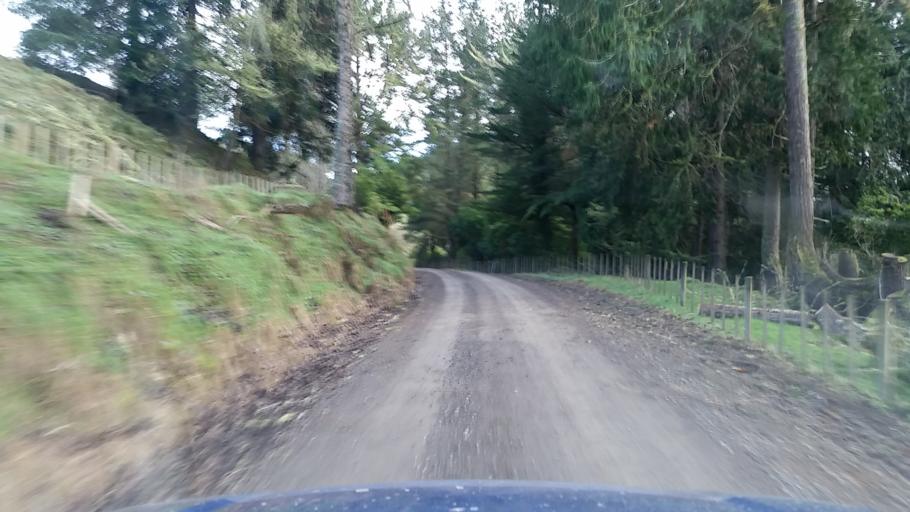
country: NZ
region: Taranaki
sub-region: New Plymouth District
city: Waitara
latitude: -39.1009
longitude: 174.8401
